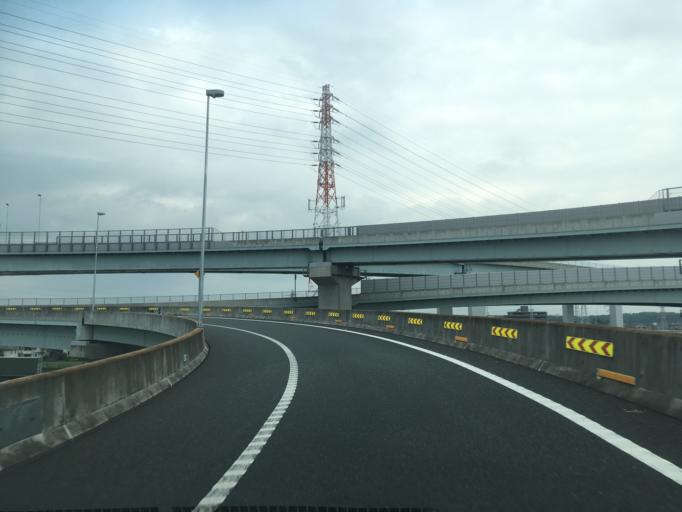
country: JP
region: Kanagawa
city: Chigasaki
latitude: 35.3498
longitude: 139.3920
